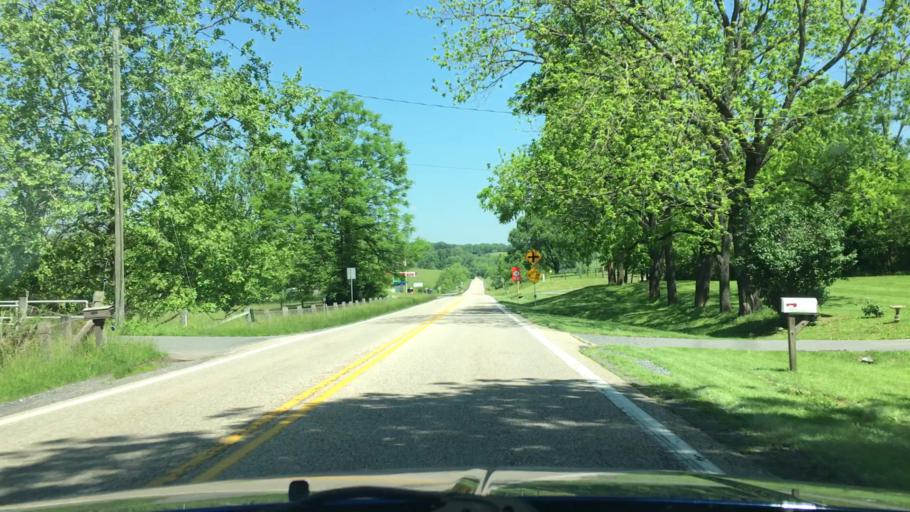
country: US
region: Virginia
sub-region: City of Staunton
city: Staunton
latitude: 38.1969
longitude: -79.1148
